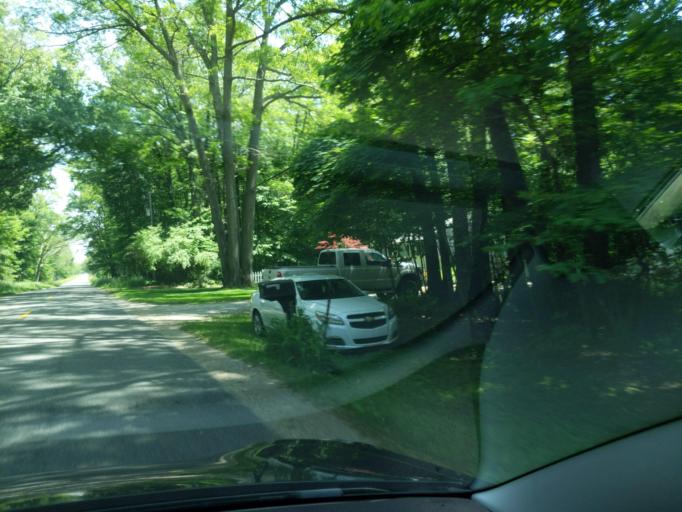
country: US
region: Michigan
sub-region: Muskegon County
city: Montague
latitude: 43.4156
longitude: -86.3881
